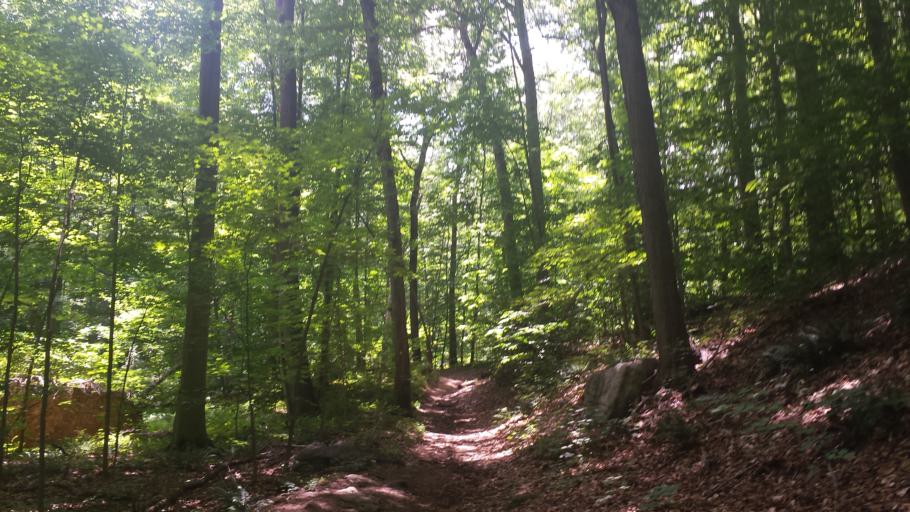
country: US
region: New York
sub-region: Westchester County
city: Scarsdale
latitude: 40.9887
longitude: -73.7555
